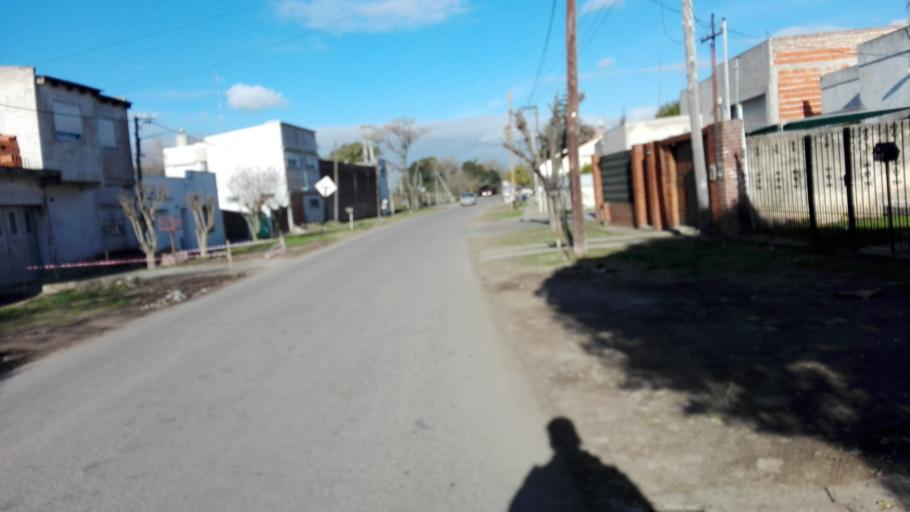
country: AR
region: Buenos Aires
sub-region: Partido de La Plata
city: La Plata
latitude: -34.9073
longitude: -58.0210
